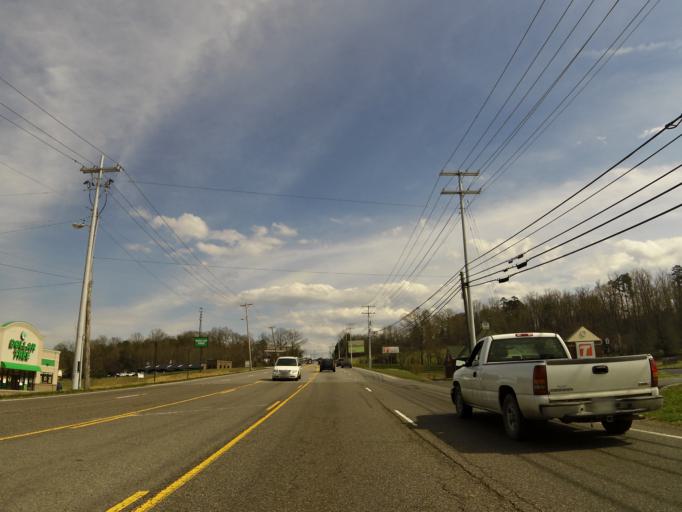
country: US
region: Tennessee
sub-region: Sevier County
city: Seymour
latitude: 35.8785
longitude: -83.7735
